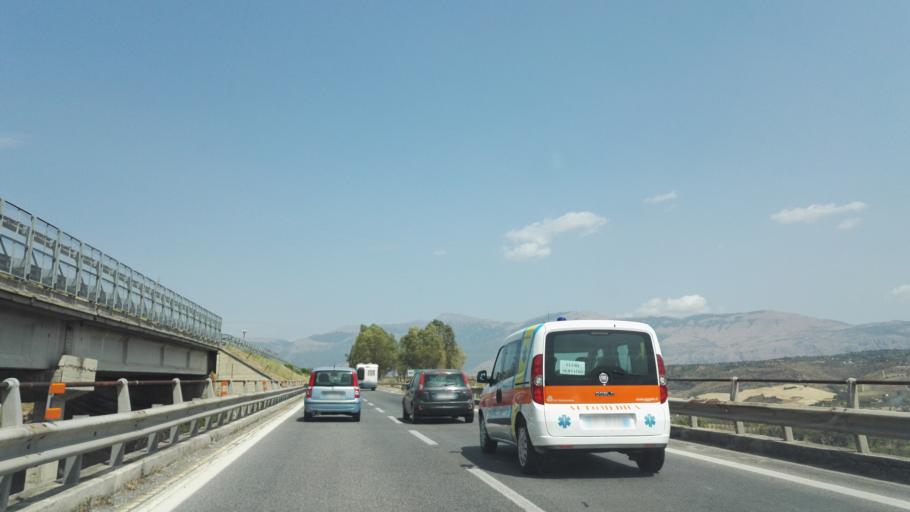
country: IT
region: Calabria
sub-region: Provincia di Cosenza
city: Firmo
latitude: 39.7469
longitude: 16.2256
